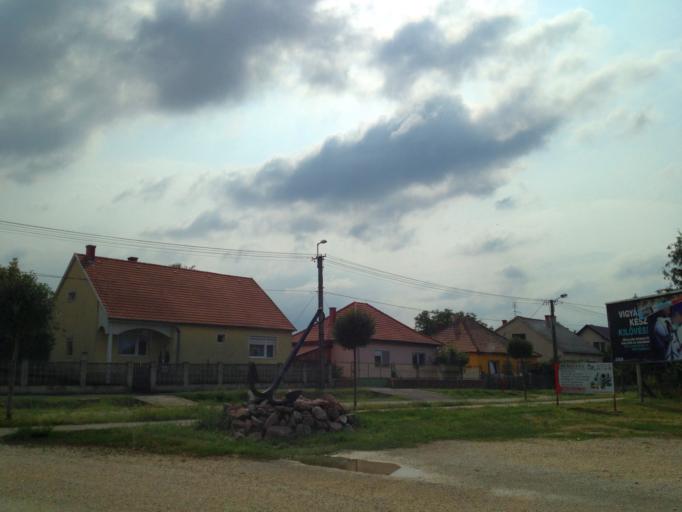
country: HU
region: Gyor-Moson-Sopron
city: Bony
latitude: 47.7333
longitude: 17.8408
